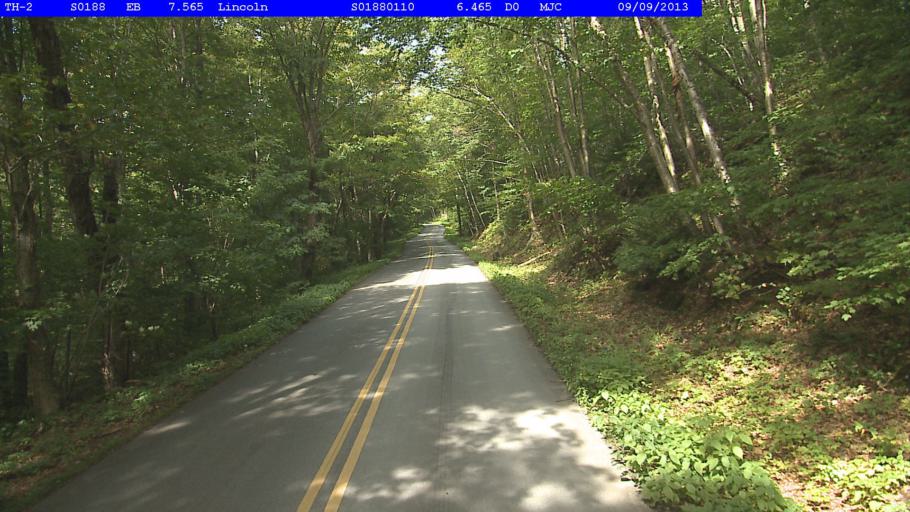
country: US
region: Vermont
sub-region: Addison County
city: Bristol
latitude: 44.0922
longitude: -72.9322
